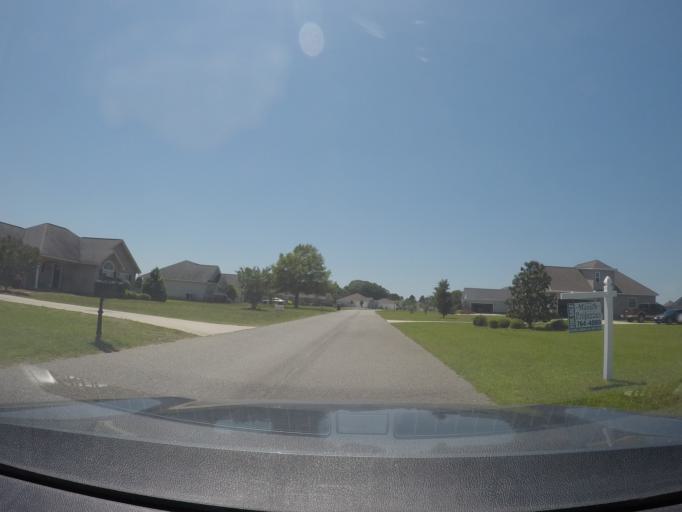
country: US
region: Georgia
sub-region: Bulloch County
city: Brooklet
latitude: 32.3566
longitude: -81.7534
